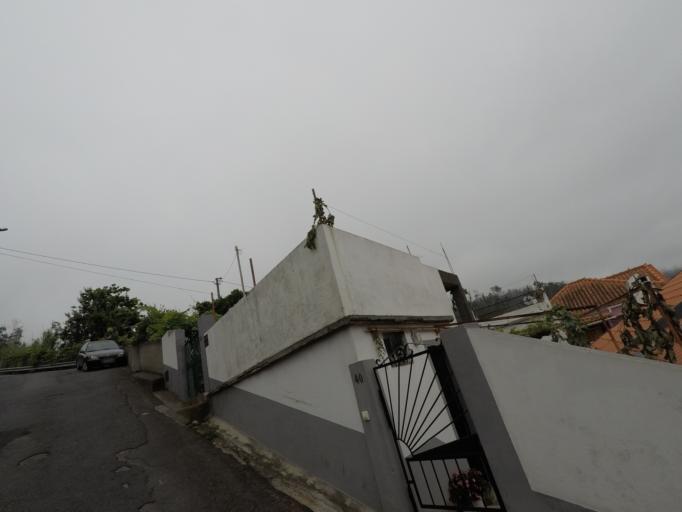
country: PT
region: Madeira
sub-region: Funchal
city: Nossa Senhora do Monte
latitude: 32.6812
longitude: -16.9379
